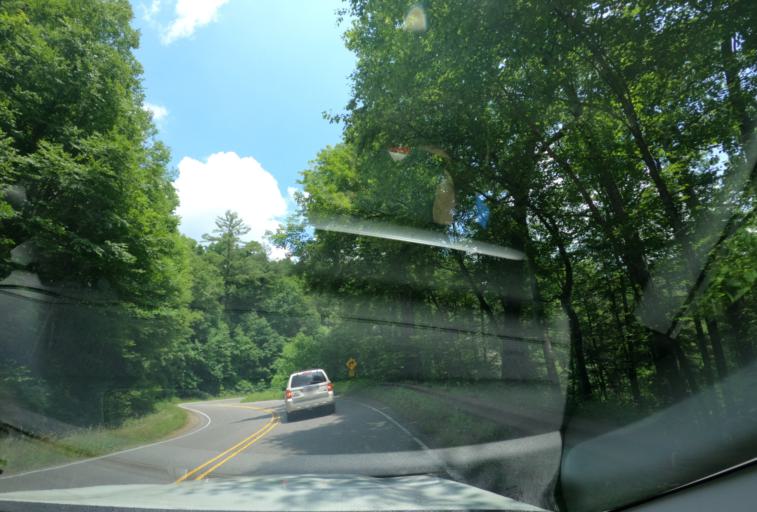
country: US
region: North Carolina
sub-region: Macon County
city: Franklin
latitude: 35.0714
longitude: -83.2338
